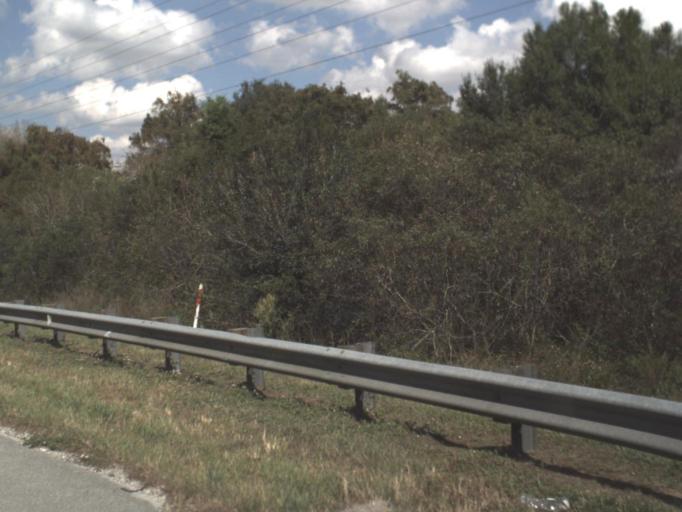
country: US
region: Florida
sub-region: Okeechobee County
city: Okeechobee
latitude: 27.3816
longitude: -80.9919
